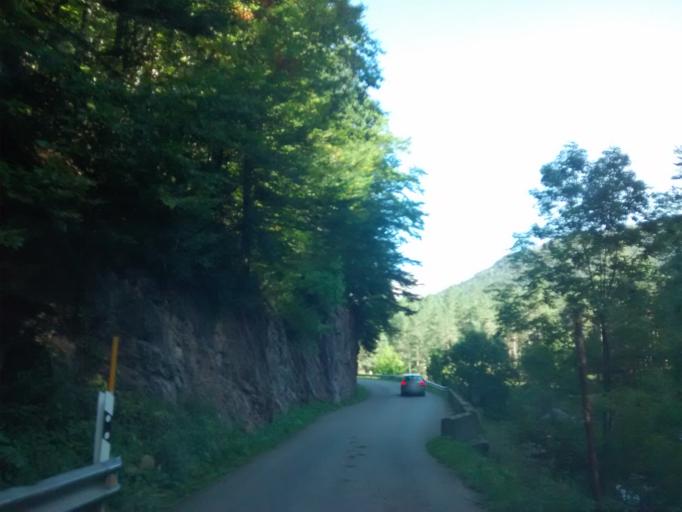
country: ES
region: Aragon
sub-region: Provincia de Huesca
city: Aragues del Puerto
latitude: 42.8289
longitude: -0.7116
